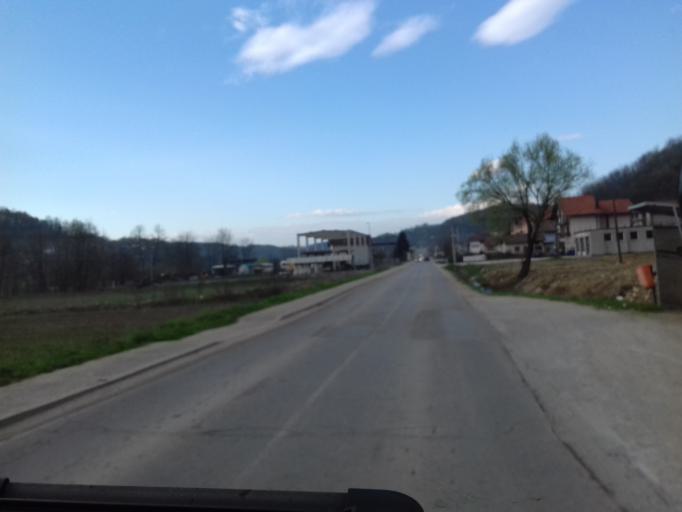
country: BA
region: Federation of Bosnia and Herzegovina
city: Tesanjka
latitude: 44.6433
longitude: 18.0191
